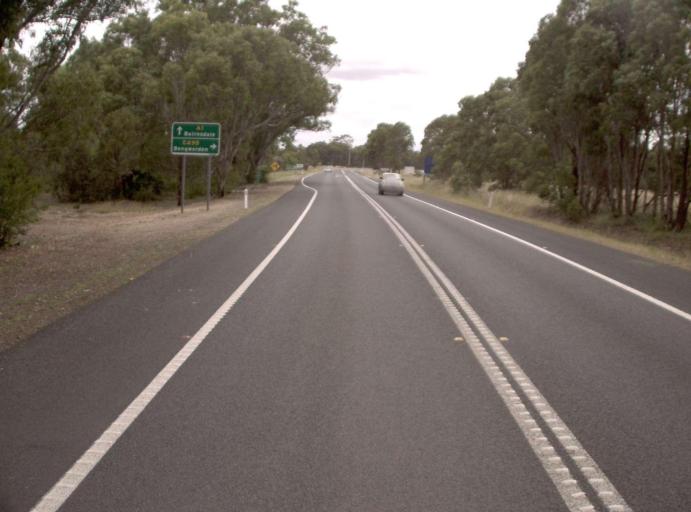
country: AU
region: Victoria
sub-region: Wellington
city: Sale
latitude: -37.9600
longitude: 147.0949
